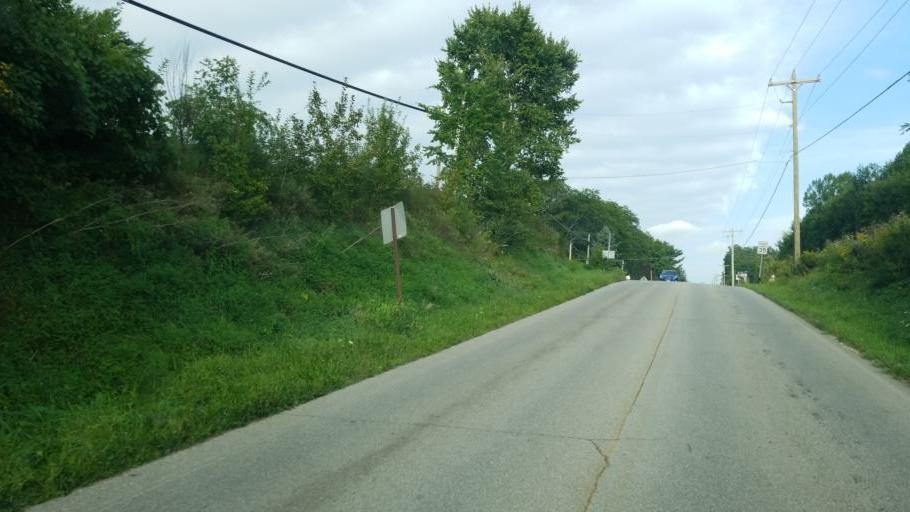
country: US
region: Ohio
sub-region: Richland County
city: Mansfield
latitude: 40.6959
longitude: -82.5052
